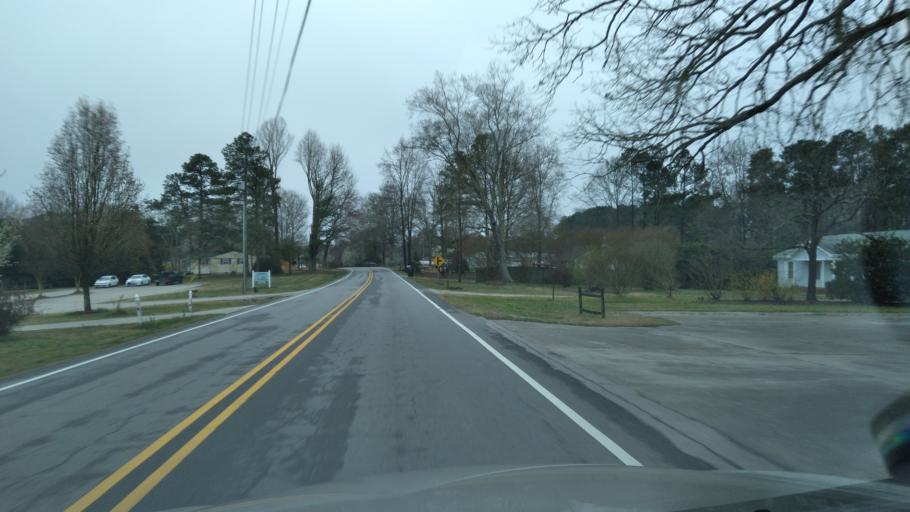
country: US
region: North Carolina
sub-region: Wake County
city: Knightdale
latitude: 35.7798
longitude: -78.4899
